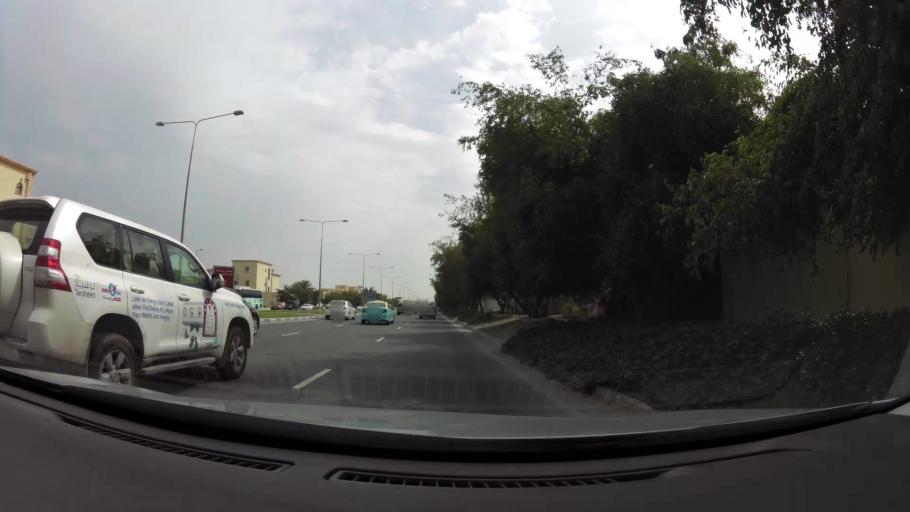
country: QA
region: Baladiyat ad Dawhah
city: Doha
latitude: 25.3412
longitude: 51.5058
